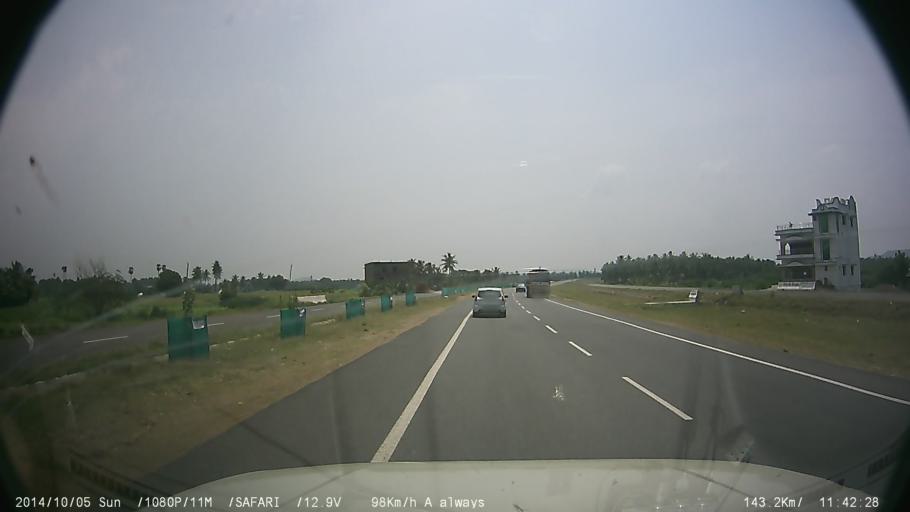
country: IN
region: Tamil Nadu
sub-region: Salem
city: Attur
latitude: 11.6029
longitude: 78.6149
